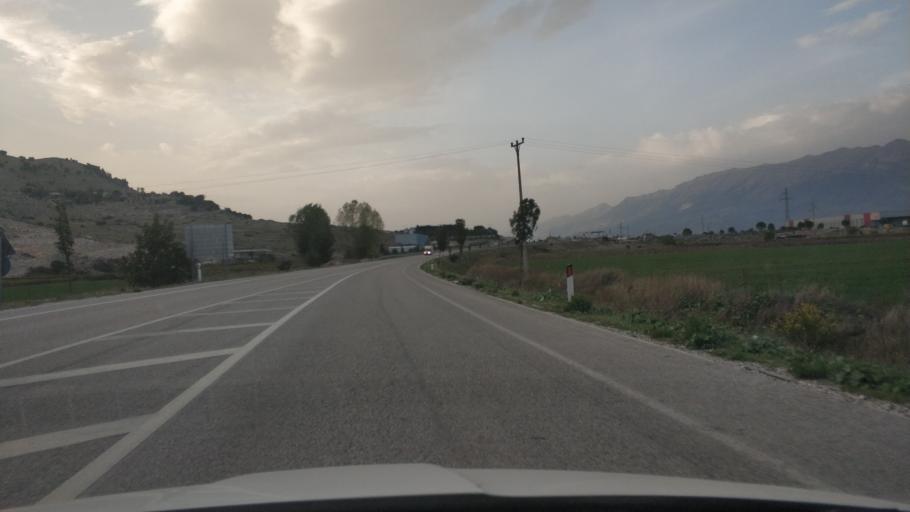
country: AL
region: Gjirokaster
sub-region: Rrethi i Gjirokastres
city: Libohove
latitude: 39.9690
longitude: 20.2378
